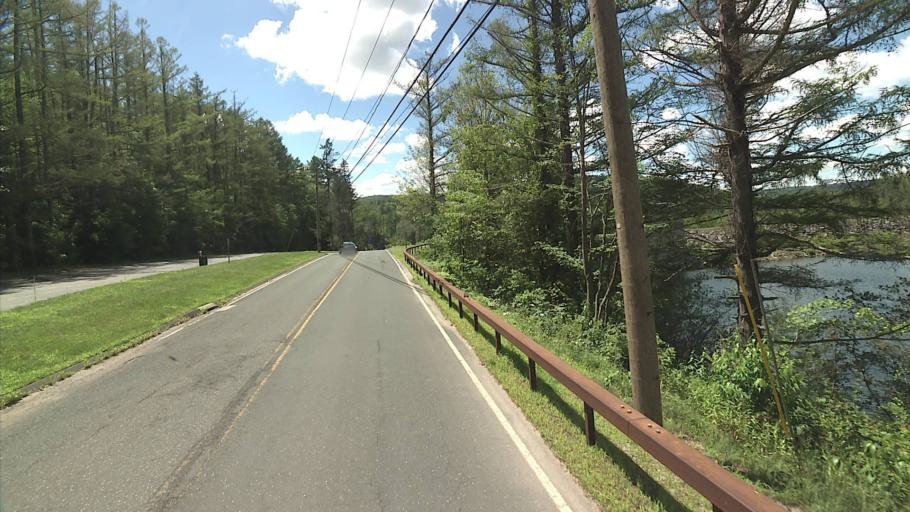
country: US
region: Connecticut
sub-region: Litchfield County
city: New Hartford Center
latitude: 41.8804
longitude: -72.9559
